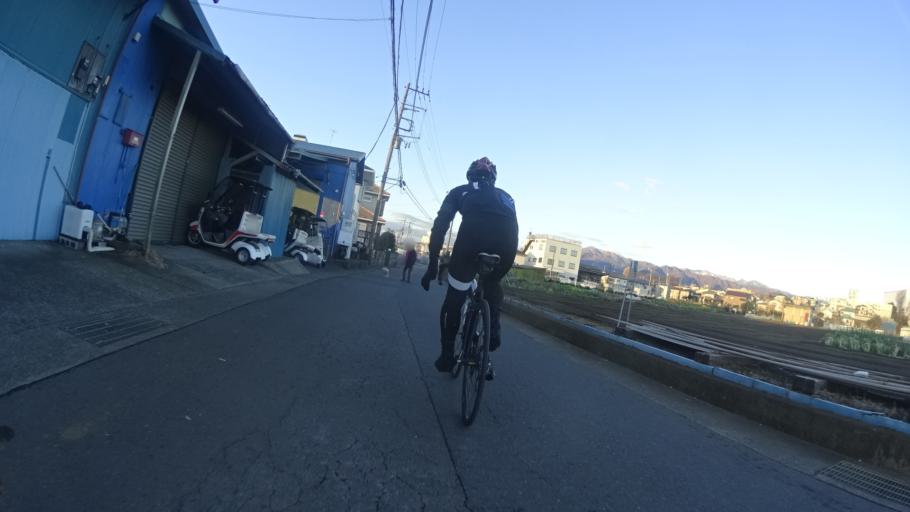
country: JP
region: Kanagawa
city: Zama
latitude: 35.4670
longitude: 139.3725
